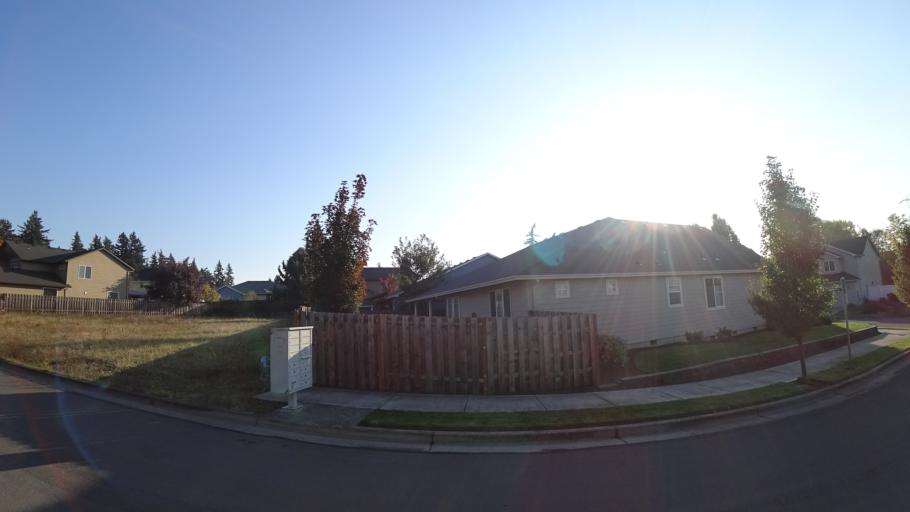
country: US
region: Oregon
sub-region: Multnomah County
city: Gresham
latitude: 45.5116
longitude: -122.4512
